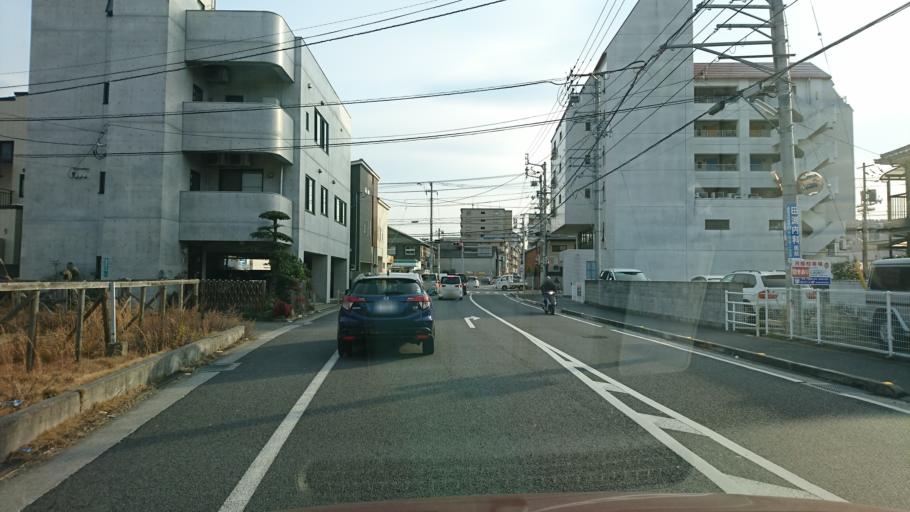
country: JP
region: Ehime
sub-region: Shikoku-chuo Shi
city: Matsuyama
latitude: 33.8528
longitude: 132.7762
